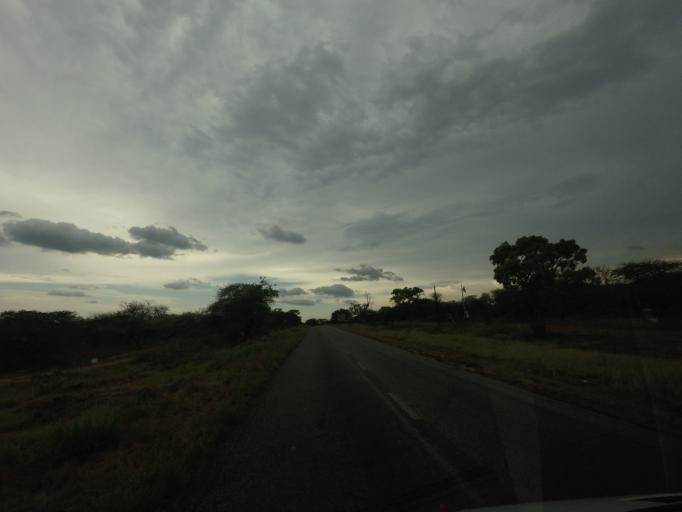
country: ZA
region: Limpopo
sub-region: Mopani District Municipality
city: Hoedspruit
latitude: -24.5129
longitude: 30.9449
